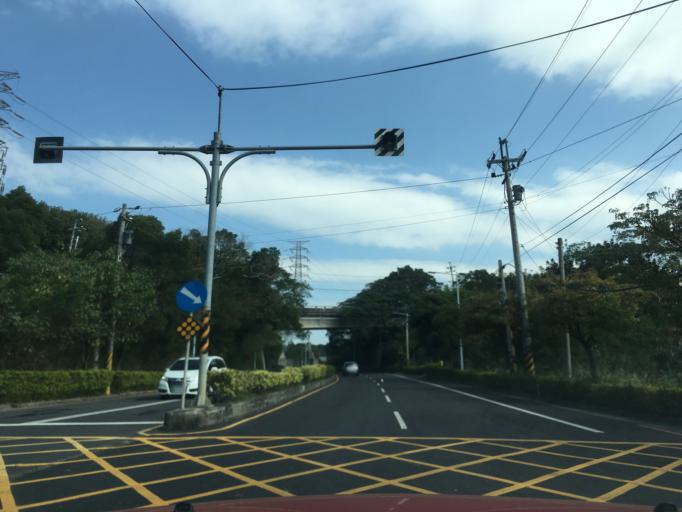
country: TW
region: Taiwan
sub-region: Hsinchu
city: Hsinchu
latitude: 24.7619
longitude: 121.0072
